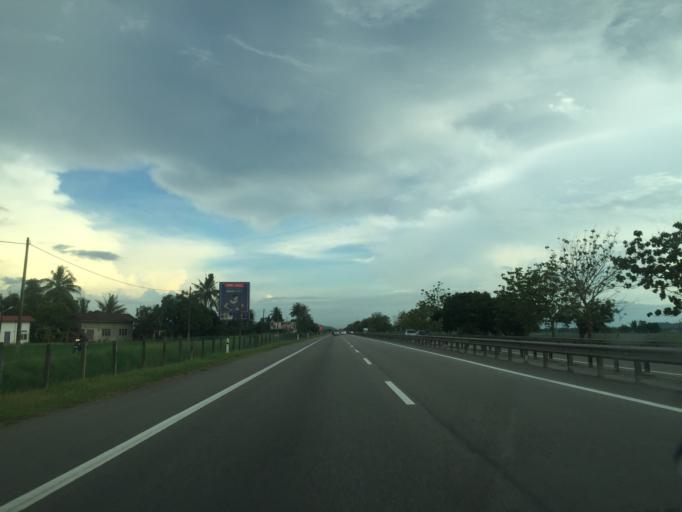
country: MY
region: Kedah
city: Alor Setar
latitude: 6.0108
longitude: 100.4194
